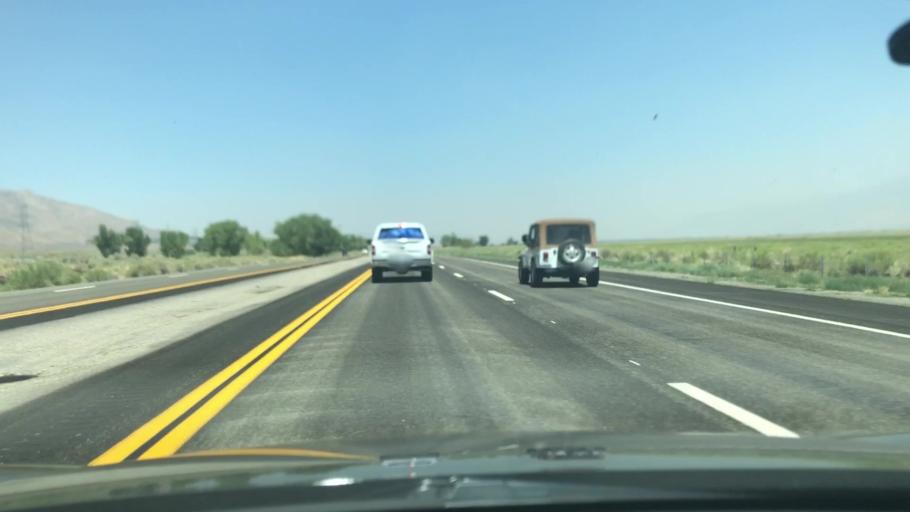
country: US
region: California
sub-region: Inyo County
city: Big Pine
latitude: 37.2358
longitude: -118.3492
